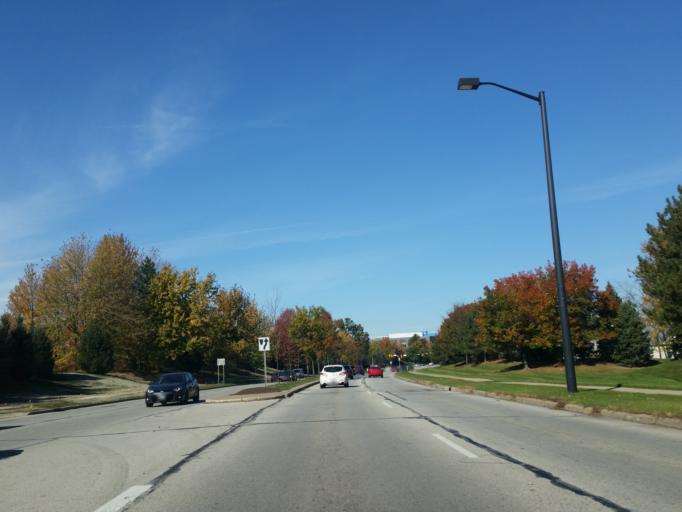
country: US
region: Ohio
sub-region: Cuyahoga County
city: Westlake
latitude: 41.4481
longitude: -81.9487
